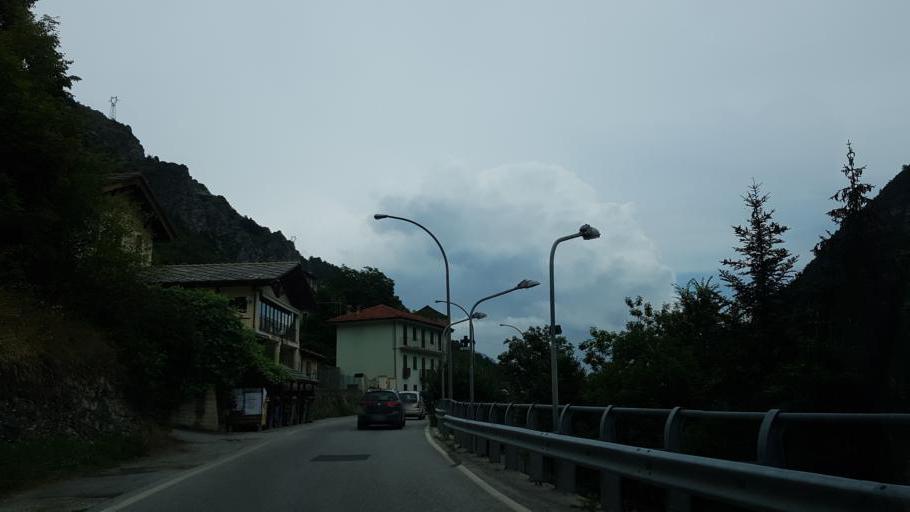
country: IT
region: Piedmont
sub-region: Provincia di Cuneo
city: Stroppo
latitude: 44.5029
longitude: 7.1273
